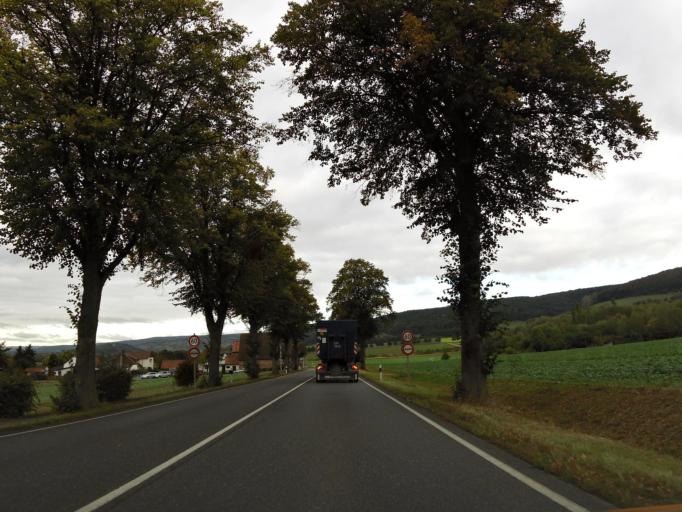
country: DE
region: Lower Saxony
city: Einbeck
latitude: 51.7795
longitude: 9.9366
